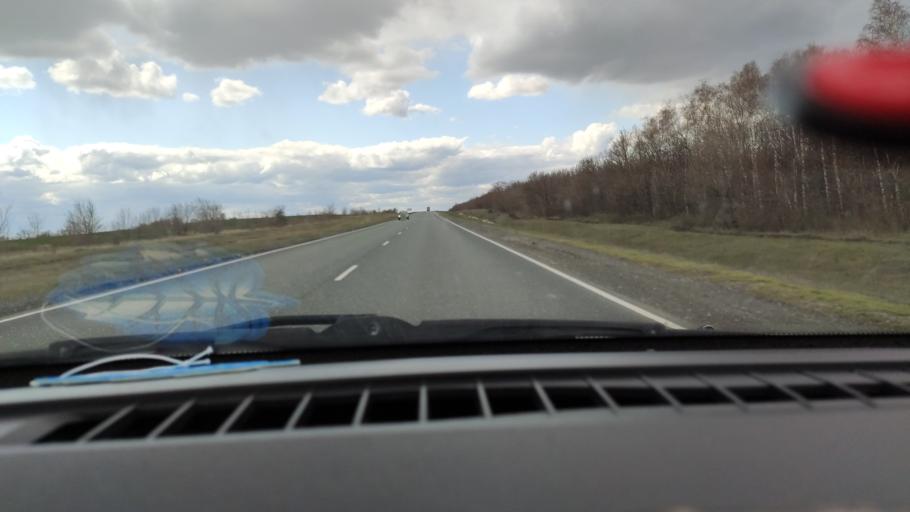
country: RU
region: Saratov
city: Balakovo
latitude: 52.1810
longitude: 47.8419
